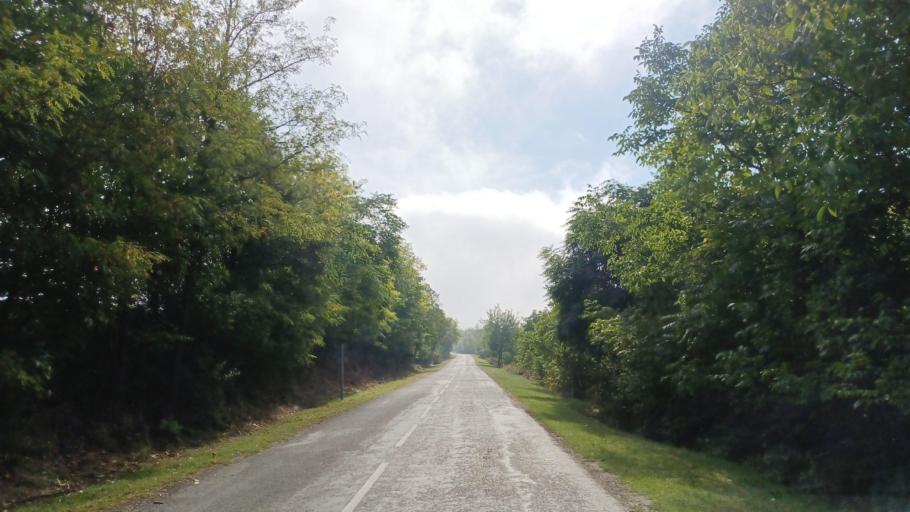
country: HU
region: Tolna
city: Pincehely
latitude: 46.6638
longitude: 18.4945
